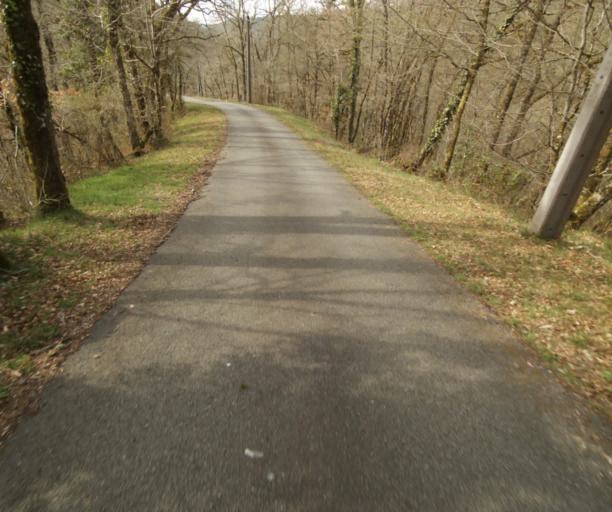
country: FR
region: Limousin
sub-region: Departement de la Correze
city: Correze
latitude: 45.4186
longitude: 1.7990
